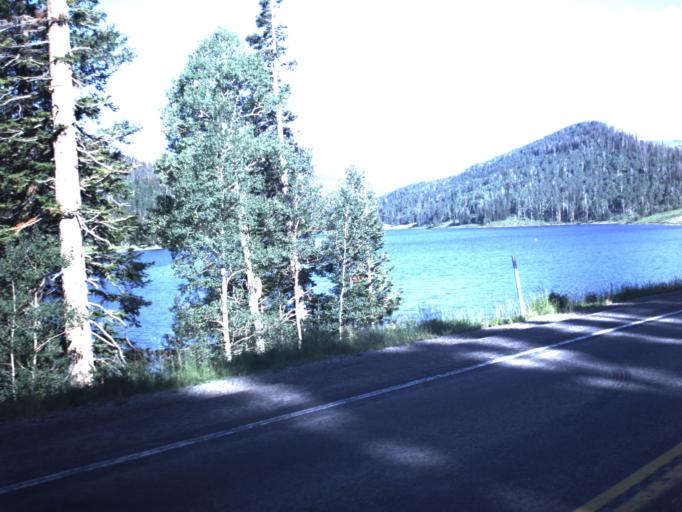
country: US
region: Utah
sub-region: Sanpete County
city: Fairview
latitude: 39.5900
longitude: -111.2635
